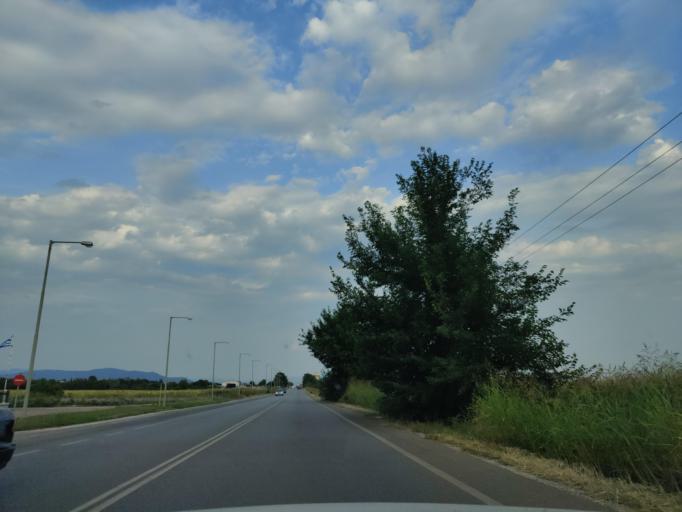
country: GR
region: East Macedonia and Thrace
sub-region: Nomos Dramas
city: Xiropotamos
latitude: 41.1653
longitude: 24.0621
